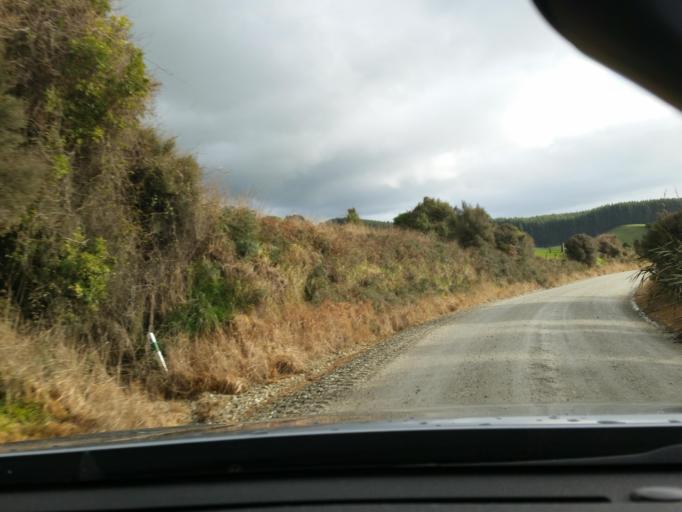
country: NZ
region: Southland
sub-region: Gore District
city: Gore
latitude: -46.5332
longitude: 168.9687
